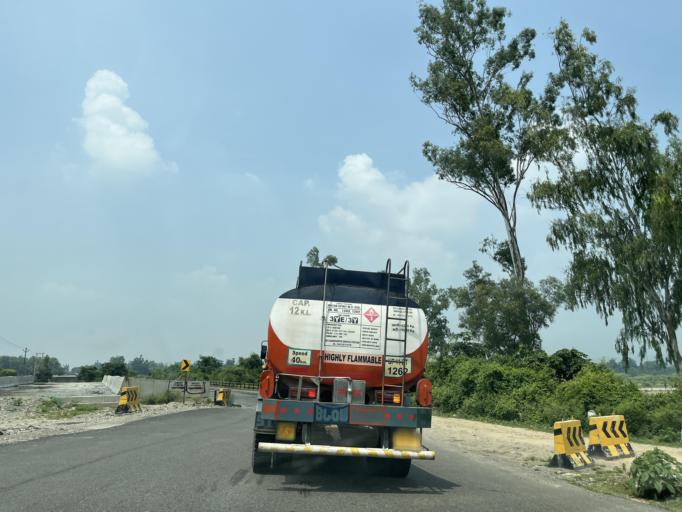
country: IN
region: Uttarakhand
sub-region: Haridwar
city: Haridwar
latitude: 29.8386
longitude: 78.1950
